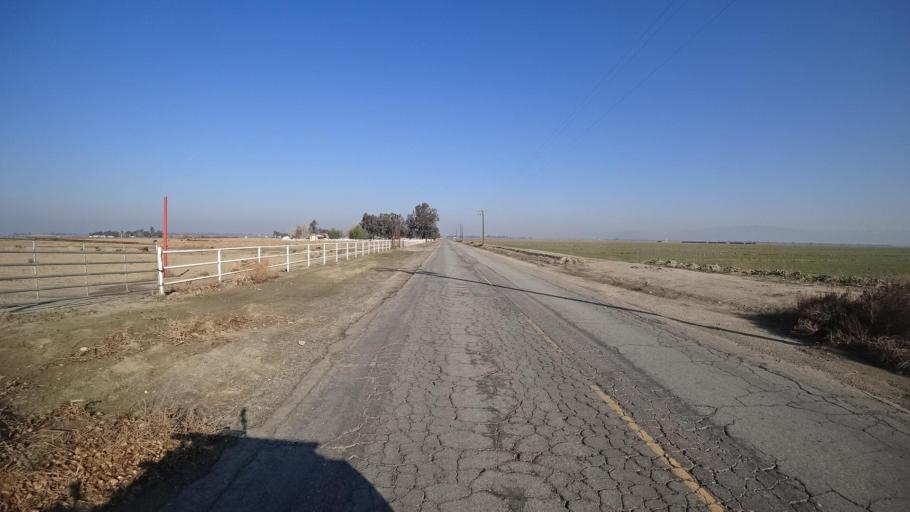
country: US
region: California
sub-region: Kern County
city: Weedpatch
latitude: 35.1512
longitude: -118.9677
